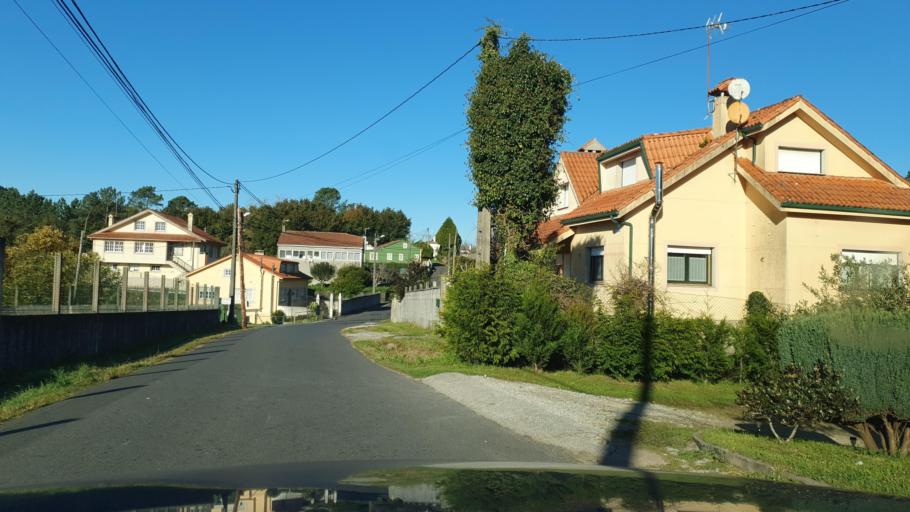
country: ES
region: Galicia
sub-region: Provincia da Coruna
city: Santiago de Compostela
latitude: 42.8324
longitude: -8.5990
